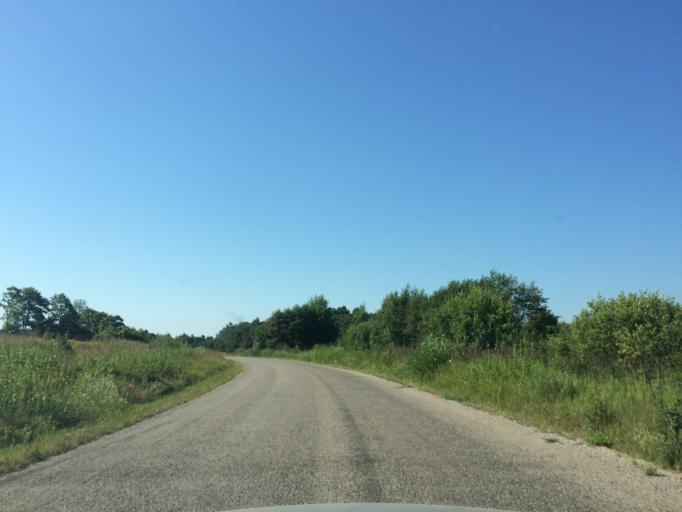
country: LV
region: Rezekne
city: Rezekne
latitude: 56.5053
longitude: 27.2997
